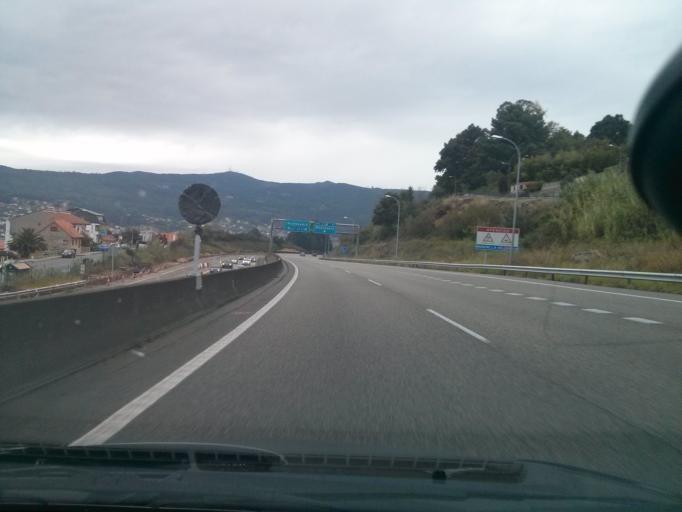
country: ES
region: Galicia
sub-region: Provincia de Pontevedra
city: Redondela
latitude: 42.2722
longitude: -8.6642
